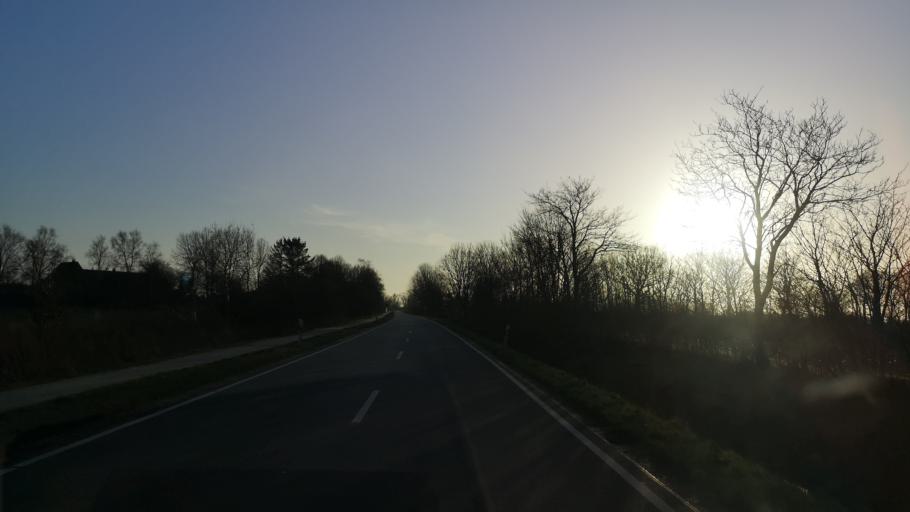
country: DE
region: Schleswig-Holstein
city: Grosssolt
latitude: 54.6876
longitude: 9.4937
